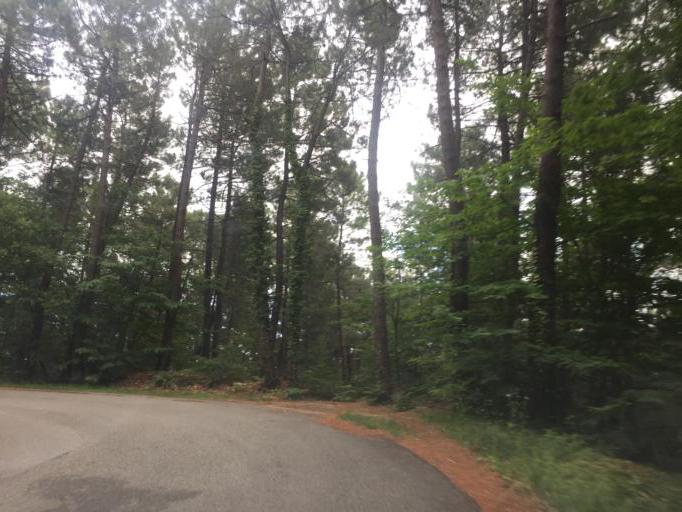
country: FR
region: Rhone-Alpes
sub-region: Departement de l'Ardeche
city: Privas
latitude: 44.7485
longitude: 4.5992
